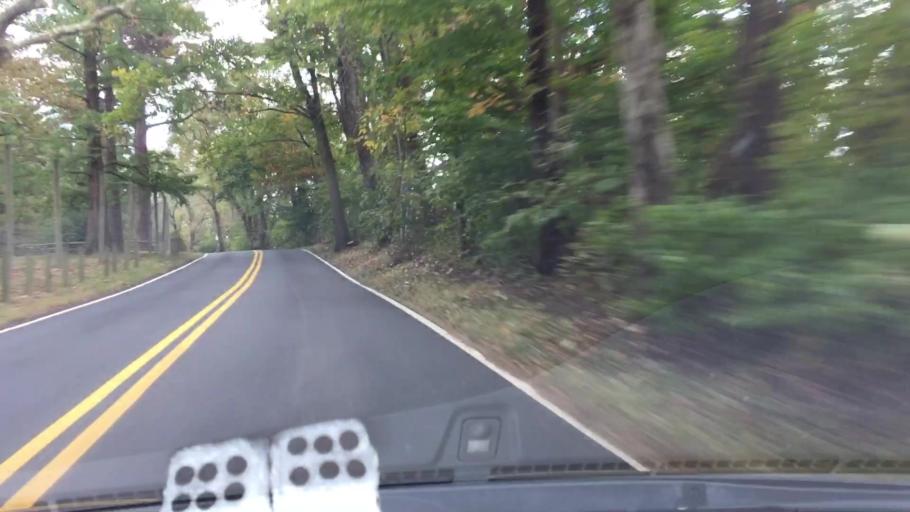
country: US
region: Pennsylvania
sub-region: Delaware County
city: Lima
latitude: 39.9319
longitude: -75.4377
